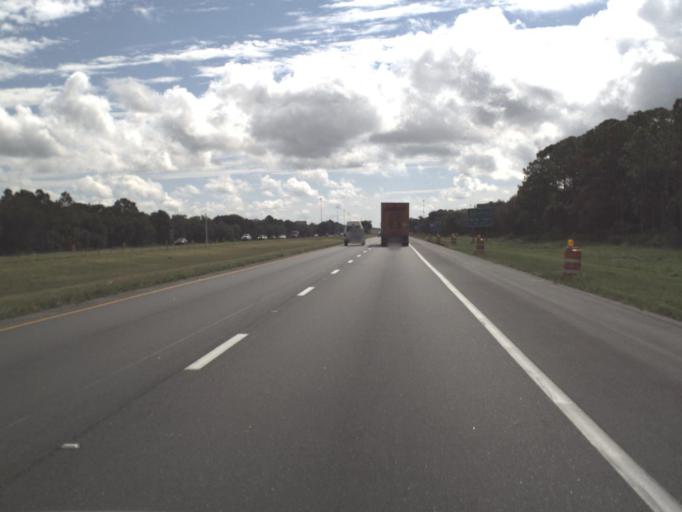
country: US
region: Florida
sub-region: Sarasota County
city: Warm Mineral Springs
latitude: 27.0993
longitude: -82.2177
